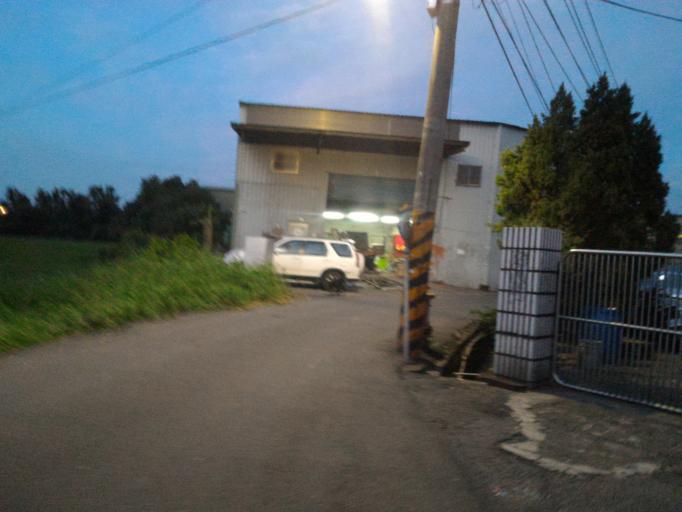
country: TW
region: Taipei
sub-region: Taipei
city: Banqiao
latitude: 24.9627
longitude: 121.4019
